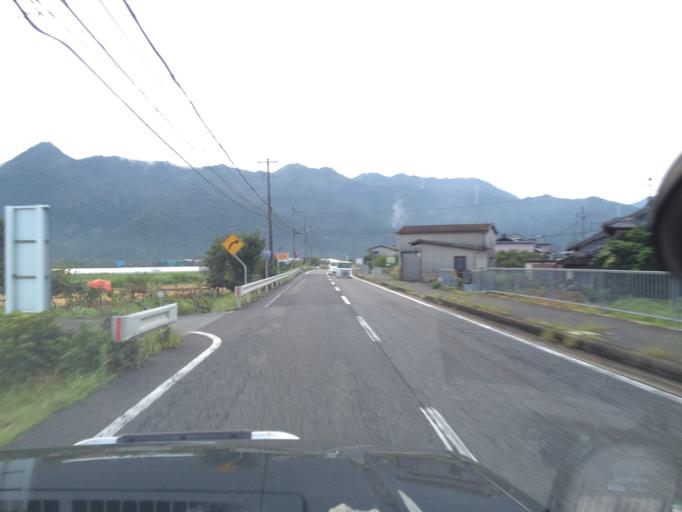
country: JP
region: Hyogo
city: Nishiwaki
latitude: 35.1028
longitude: 134.9953
